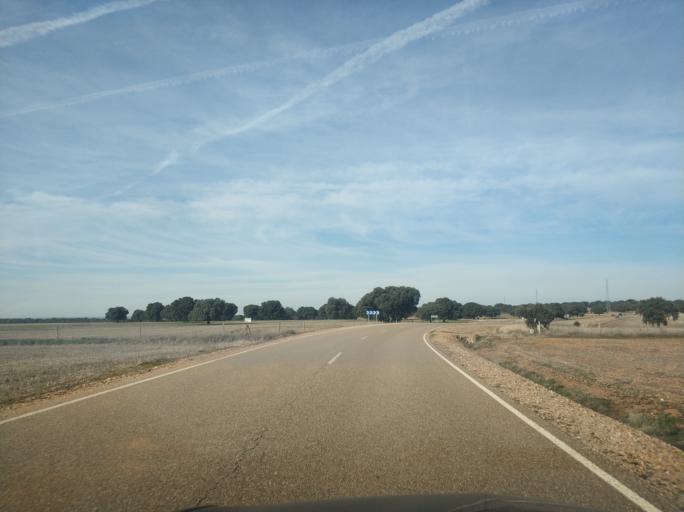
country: ES
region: Castille and Leon
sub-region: Provincia de Salamanca
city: Parada de Arriba
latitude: 40.9960
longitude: -5.8195
